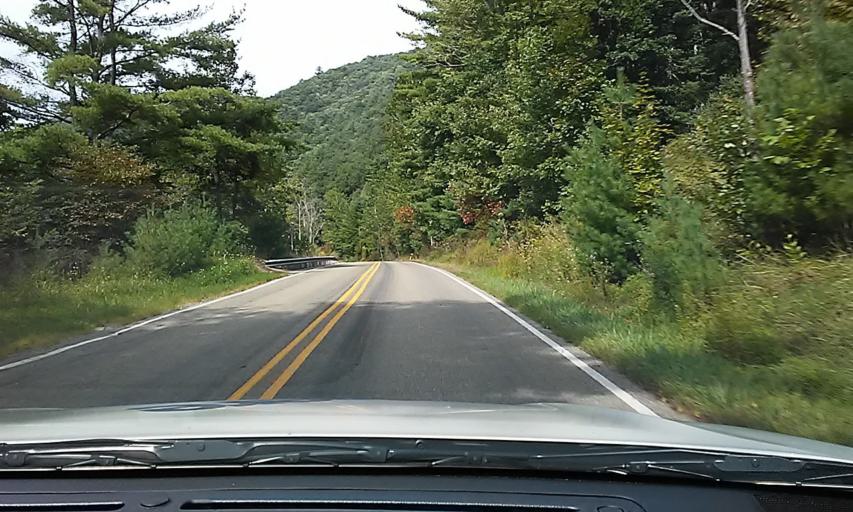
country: US
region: Pennsylvania
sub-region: Cameron County
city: Emporium
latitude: 41.3430
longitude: -78.2862
